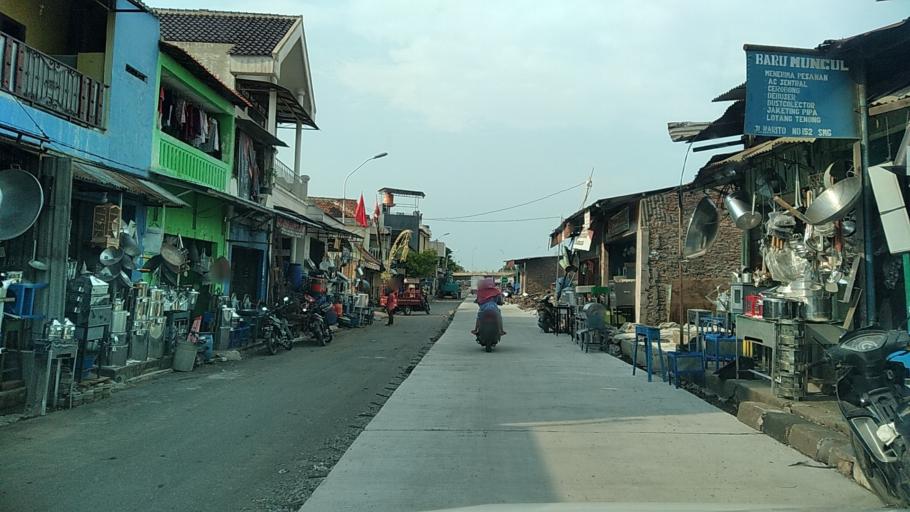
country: ID
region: Central Java
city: Semarang
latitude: -6.9746
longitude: 110.4419
